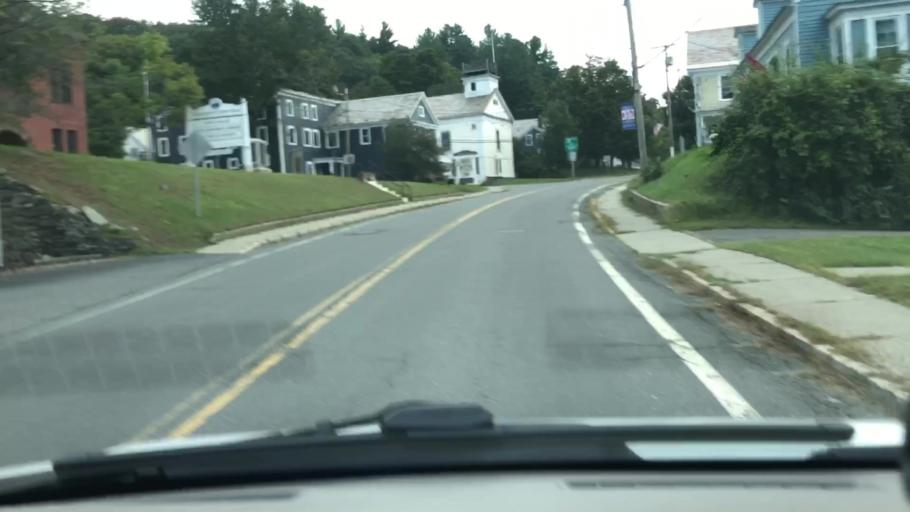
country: US
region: Massachusetts
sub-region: Franklin County
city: Charlemont
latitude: 42.6280
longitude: -72.8712
